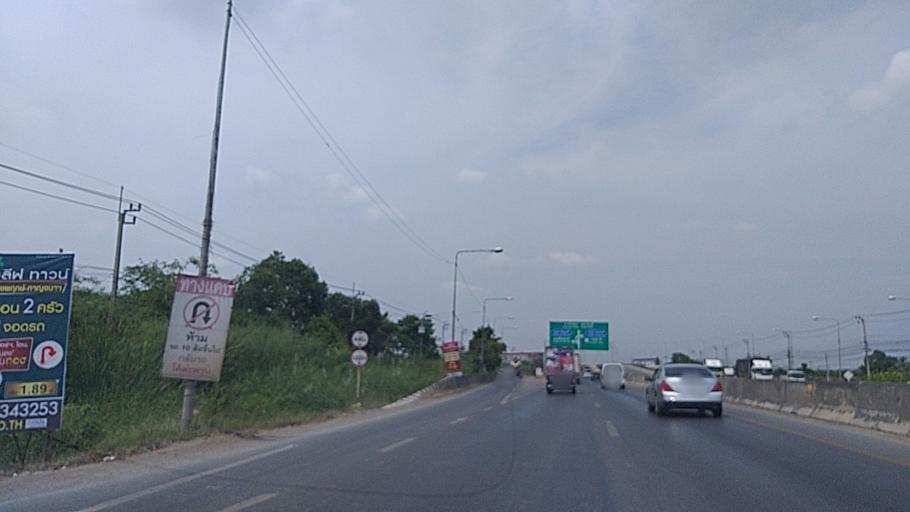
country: TH
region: Nonthaburi
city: Pak Kret
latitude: 13.9527
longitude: 100.4716
